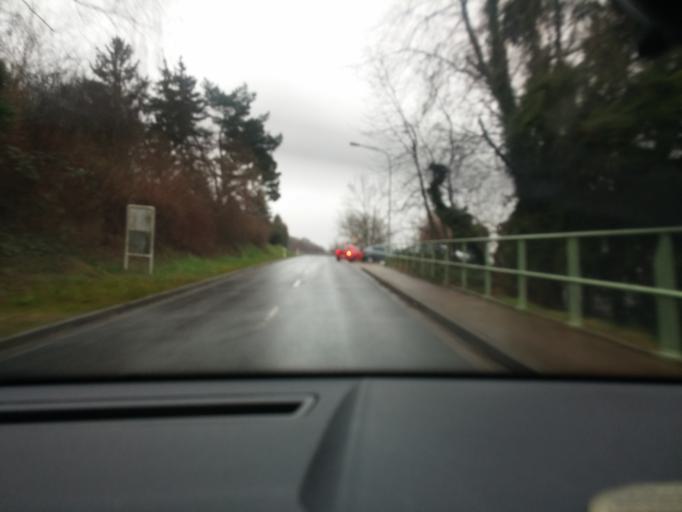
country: DE
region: Hesse
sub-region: Regierungsbezirk Darmstadt
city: Brensbach
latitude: 49.7672
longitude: 8.8831
